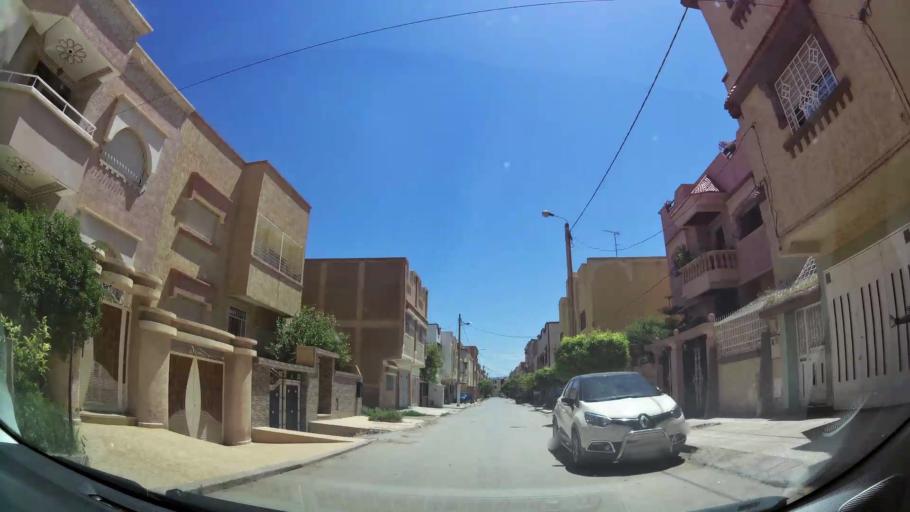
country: MA
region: Oriental
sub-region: Oujda-Angad
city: Oujda
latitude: 34.6669
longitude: -1.8934
